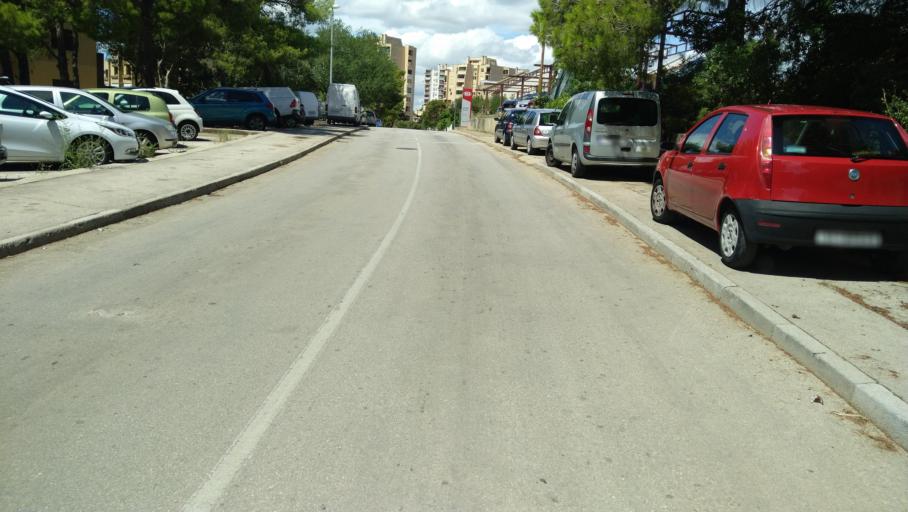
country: HR
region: Sibensko-Kniniska
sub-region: Grad Sibenik
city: Sibenik
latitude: 43.7213
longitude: 15.9118
